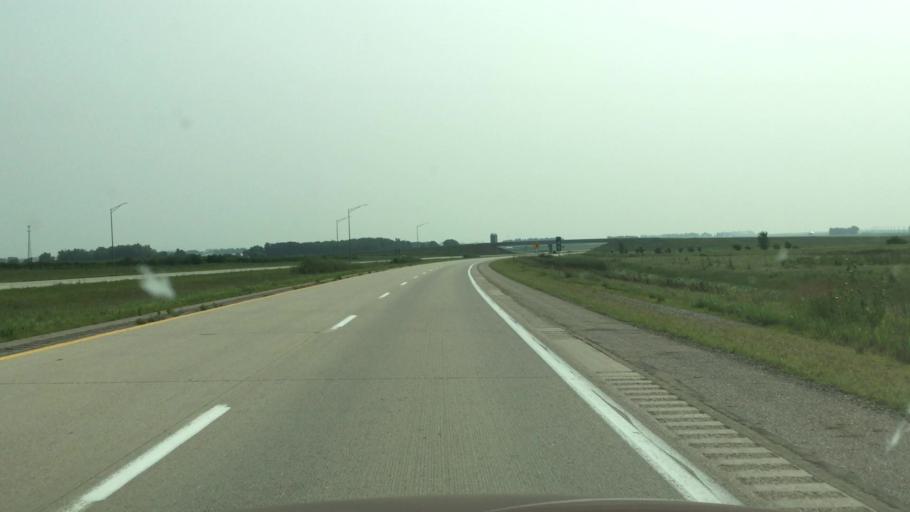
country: US
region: Iowa
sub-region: Osceola County
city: Sibley
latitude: 43.3827
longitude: -95.7487
